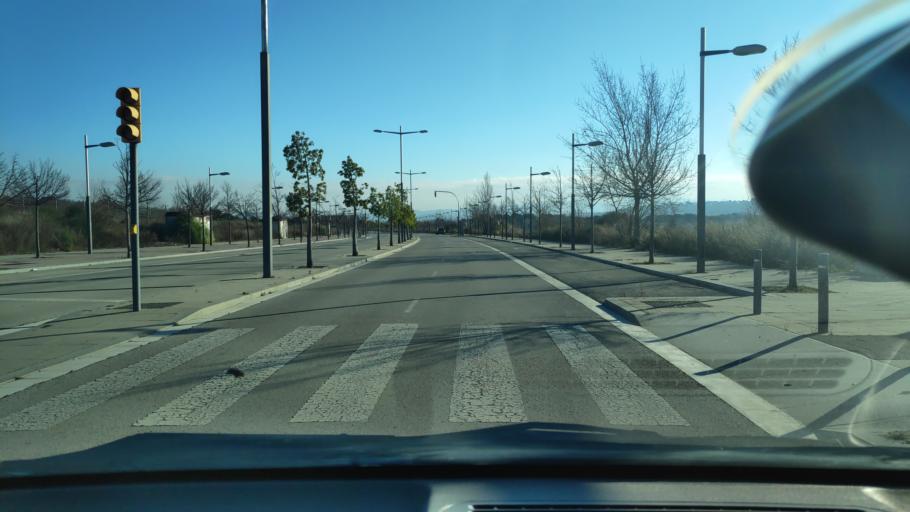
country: ES
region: Catalonia
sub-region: Provincia de Barcelona
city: Sant Quirze del Valles
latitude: 41.5451
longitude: 2.0802
